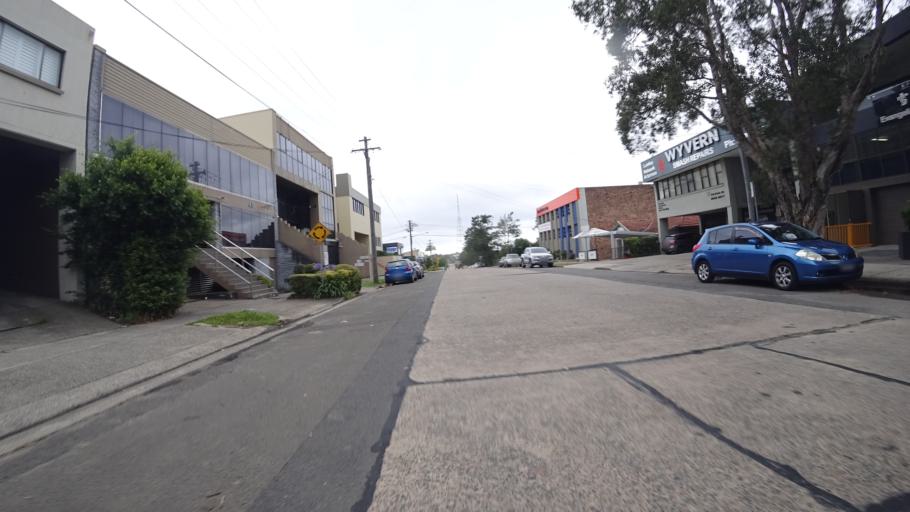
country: AU
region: New South Wales
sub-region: Willoughby
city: Artarmon
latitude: -33.8172
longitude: 151.1837
